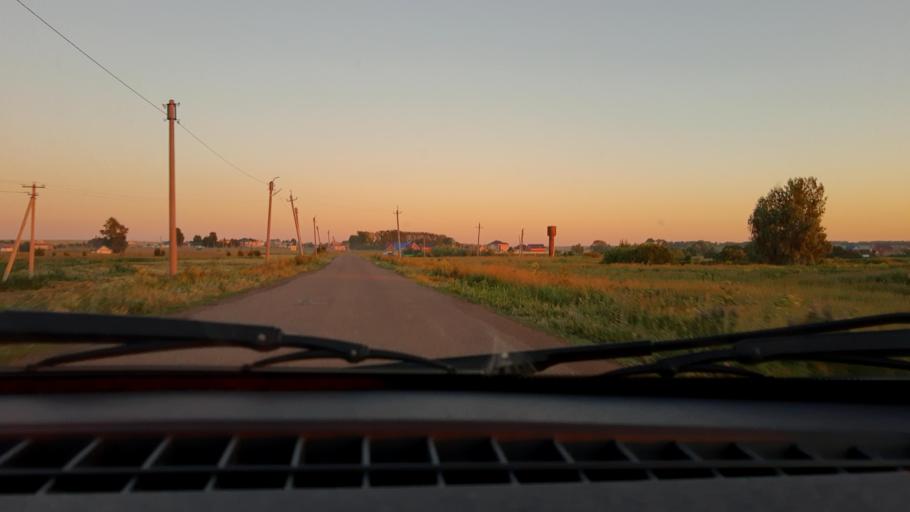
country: RU
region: Bashkortostan
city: Asanovo
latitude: 54.8973
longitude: 55.6264
